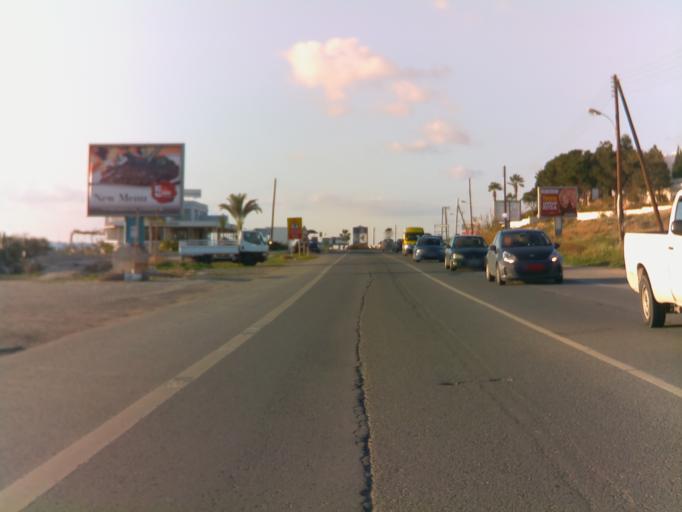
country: CY
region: Pafos
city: Chlorakas
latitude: 34.7876
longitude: 32.4043
